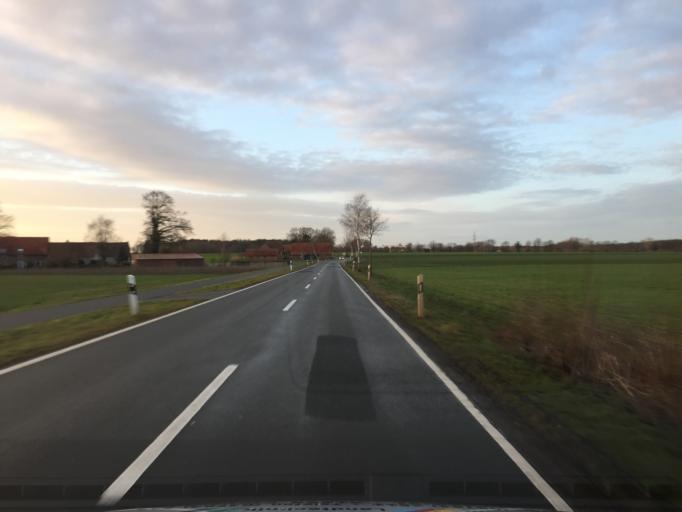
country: DE
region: Lower Saxony
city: Raddestorf
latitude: 52.4509
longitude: 8.9482
